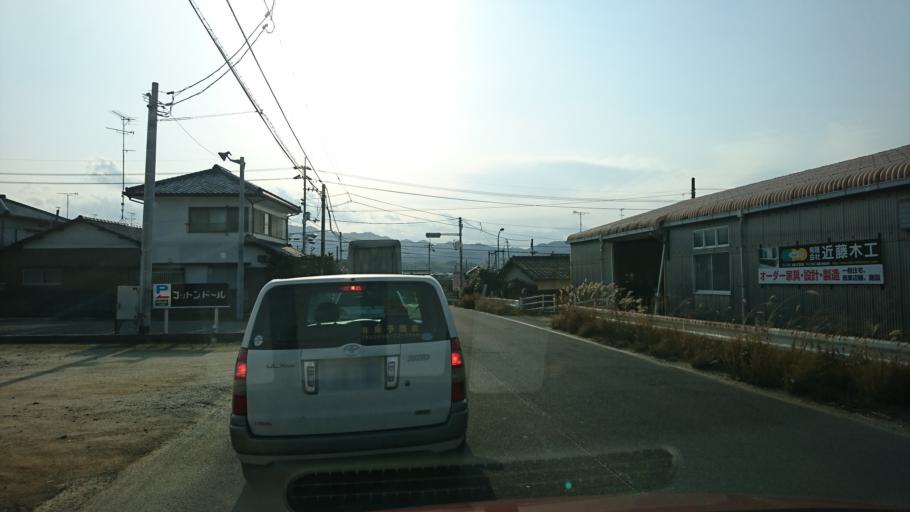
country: JP
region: Ehime
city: Saijo
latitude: 34.0306
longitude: 133.0159
